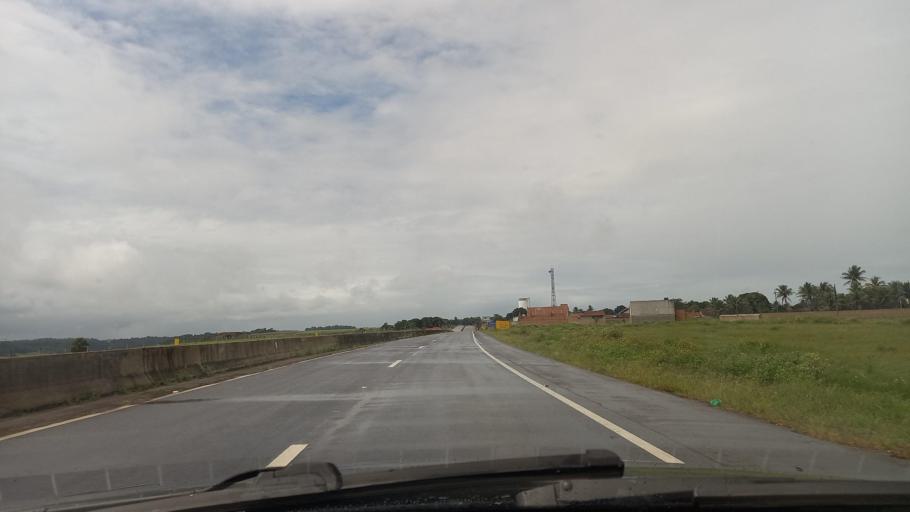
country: BR
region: Alagoas
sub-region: Campo Alegre
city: Campo Alegre
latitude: -9.8012
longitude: -36.2792
